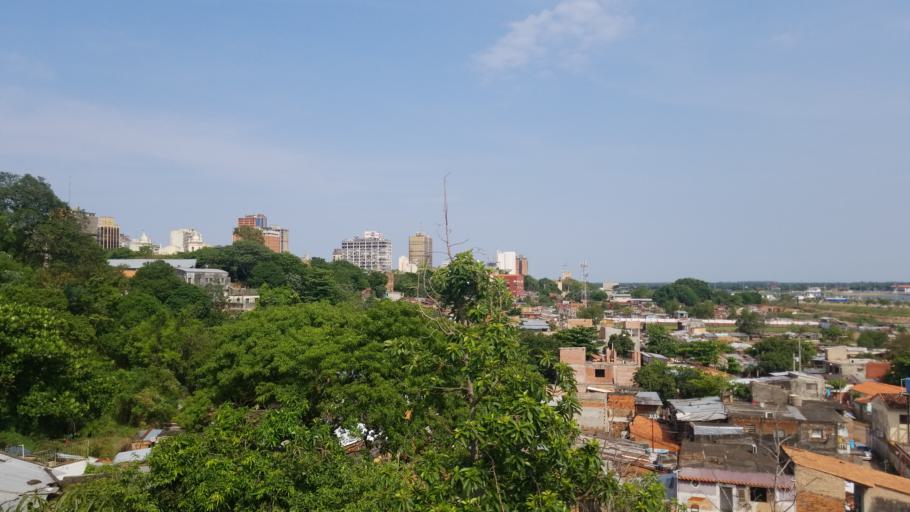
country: PY
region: Asuncion
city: Asuncion
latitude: -25.2814
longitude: -57.6291
